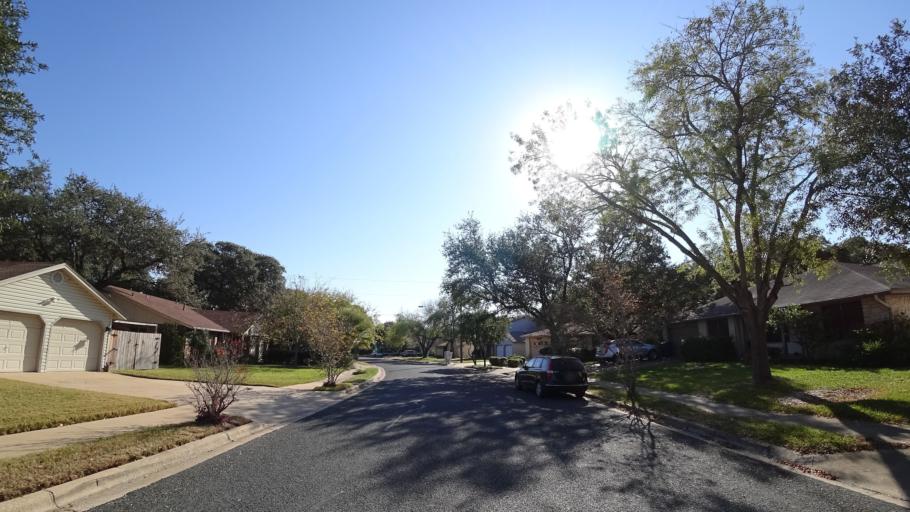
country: US
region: Texas
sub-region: Travis County
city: Shady Hollow
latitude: 30.2258
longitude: -97.8405
